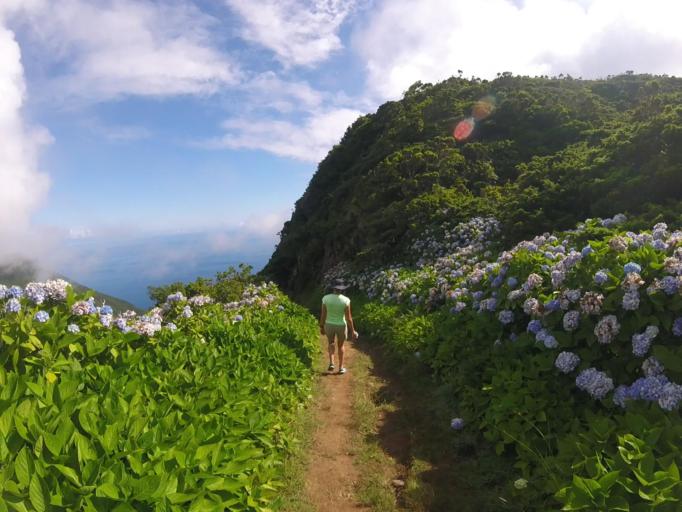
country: PT
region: Azores
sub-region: Sao Roque do Pico
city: Sao Roque do Pico
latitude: 38.5998
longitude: -27.9223
